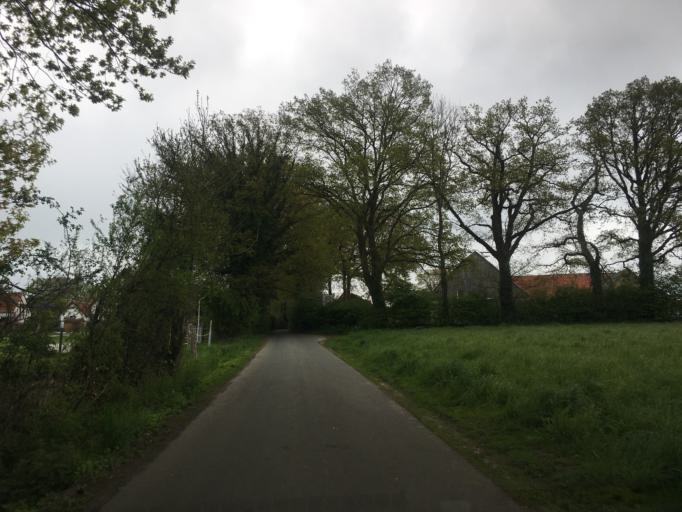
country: DE
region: North Rhine-Westphalia
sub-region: Regierungsbezirk Munster
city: Steinfurt
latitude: 52.1438
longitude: 7.3170
